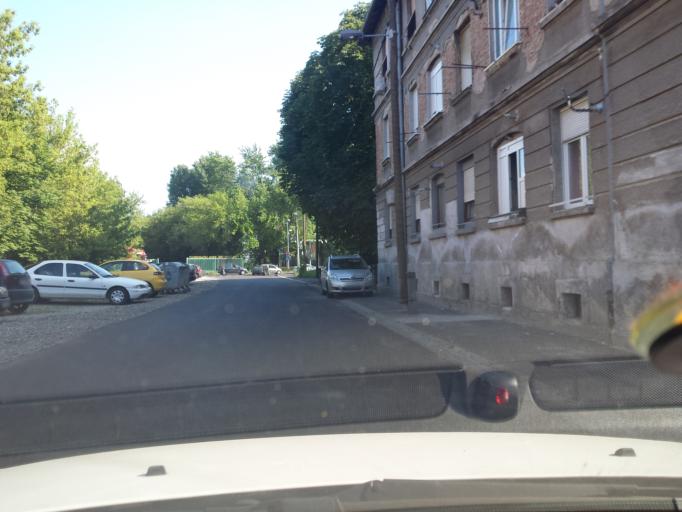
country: HR
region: Grad Zagreb
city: Zagreb - Centar
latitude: 45.8080
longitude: 15.9442
